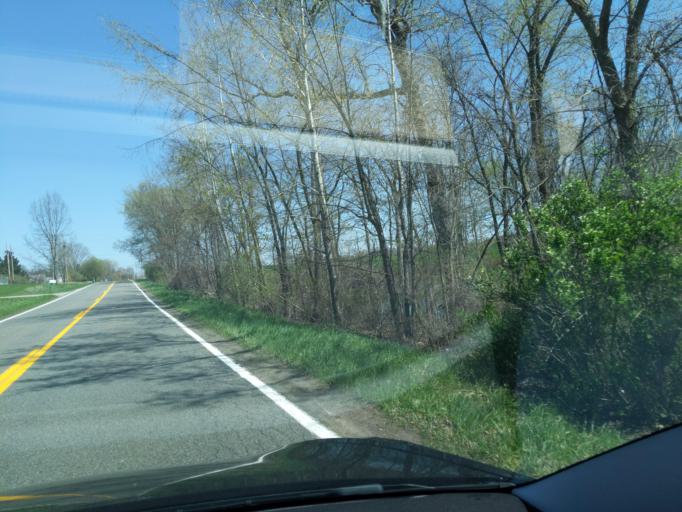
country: US
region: Michigan
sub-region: Ingham County
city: Stockbridge
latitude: 42.4461
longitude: -84.0901
